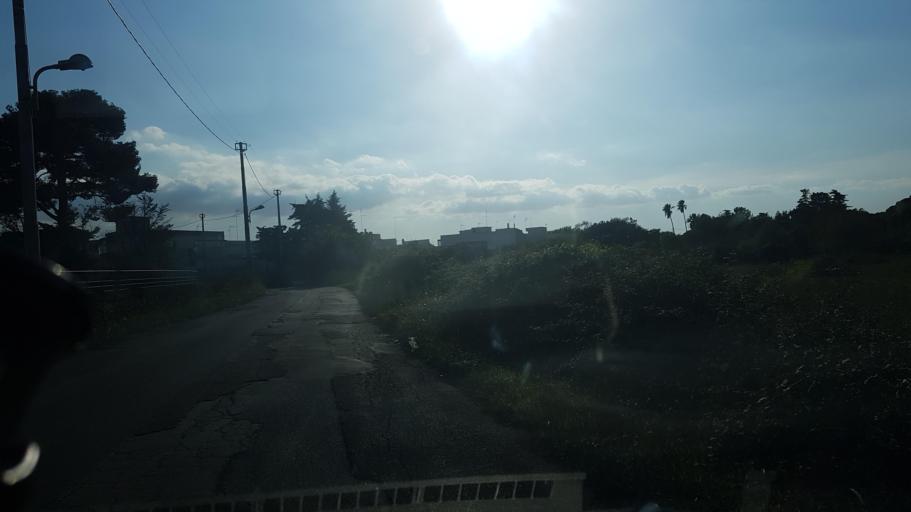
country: IT
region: Apulia
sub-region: Provincia di Brindisi
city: Mesagne
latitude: 40.5675
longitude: 17.8039
